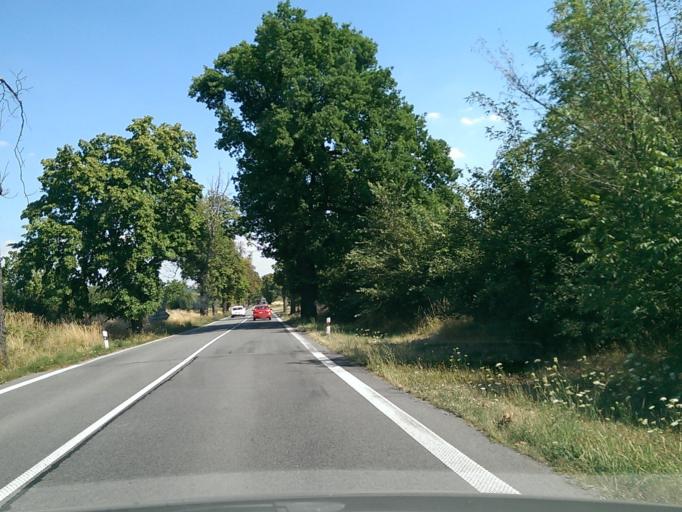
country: CZ
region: South Moravian
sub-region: Okres Breclav
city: Mikulov
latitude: 48.7985
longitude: 16.6520
